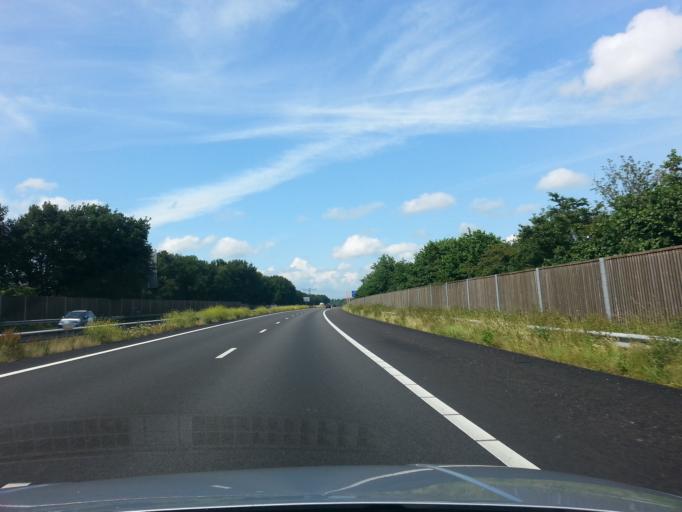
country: NL
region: Limburg
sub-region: Gemeente Venray
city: Venray
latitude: 51.5269
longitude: 6.0002
